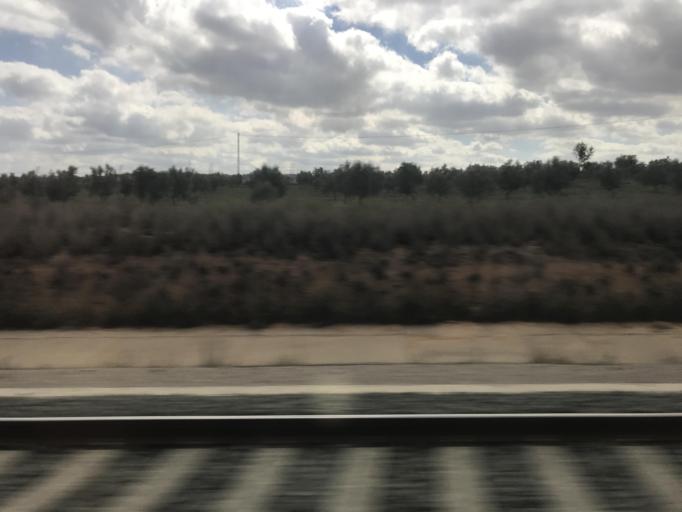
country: ES
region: Castille-La Mancha
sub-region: Provincia de Albacete
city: Almansa
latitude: 38.8855
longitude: -1.1403
